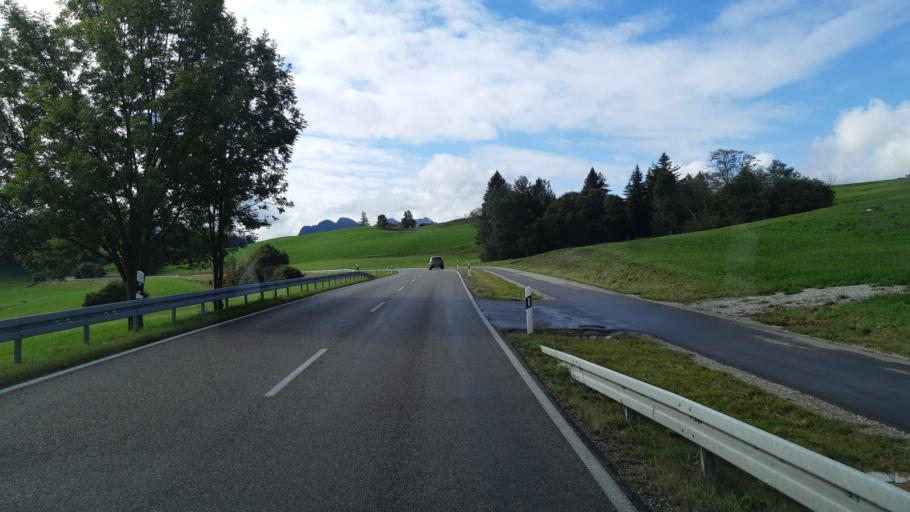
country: DE
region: Bavaria
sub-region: Swabia
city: Eisenberg
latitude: 47.6084
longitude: 10.5960
